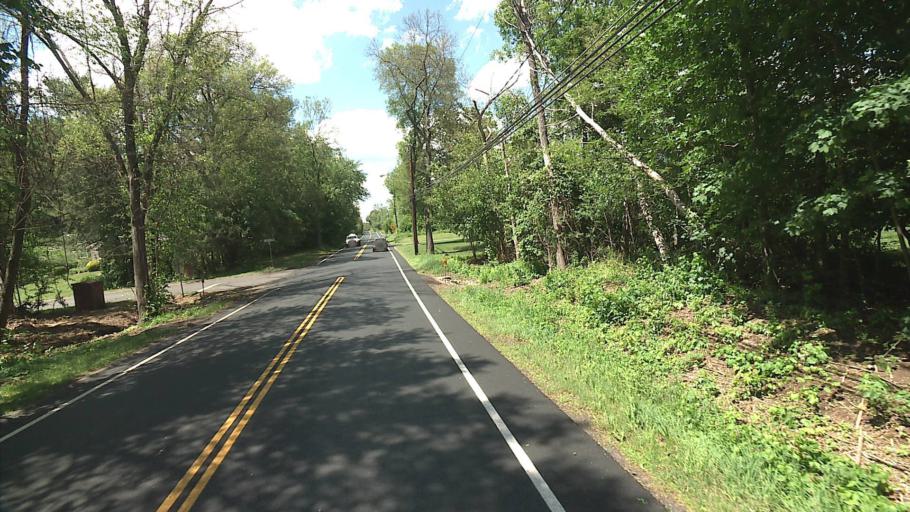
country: US
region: Connecticut
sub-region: Tolland County
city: Somers
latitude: 42.0004
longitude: -72.4336
